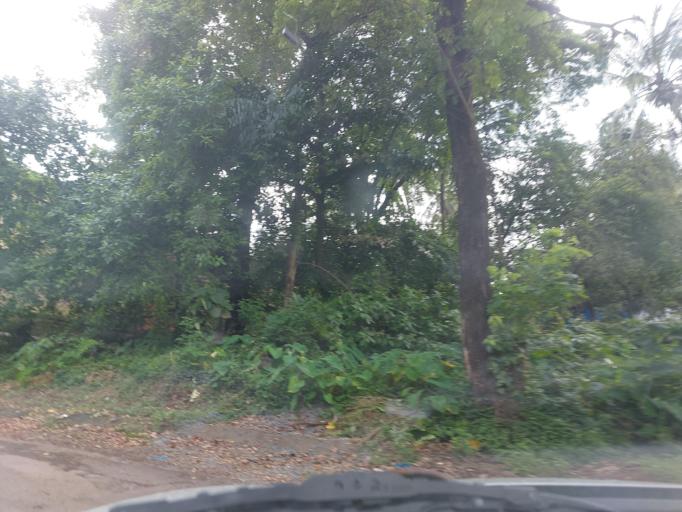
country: IN
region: Goa
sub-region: North Goa
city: Ponda
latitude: 15.3996
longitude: 74.0004
